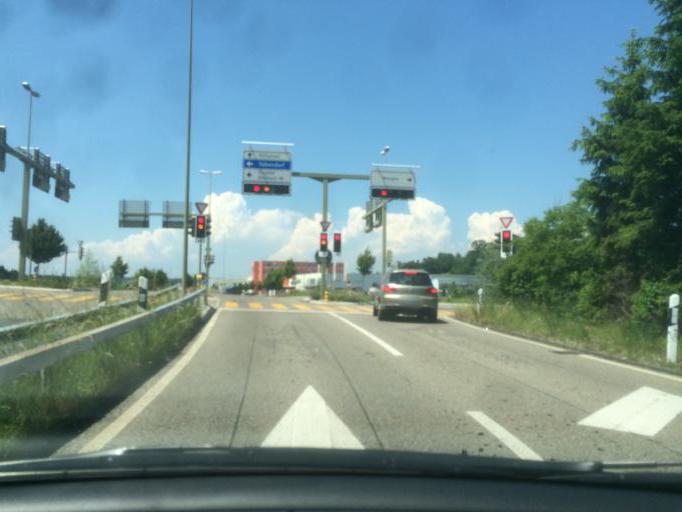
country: CH
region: Zurich
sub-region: Bezirk Uster
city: Wangen
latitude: 47.4113
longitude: 8.6369
